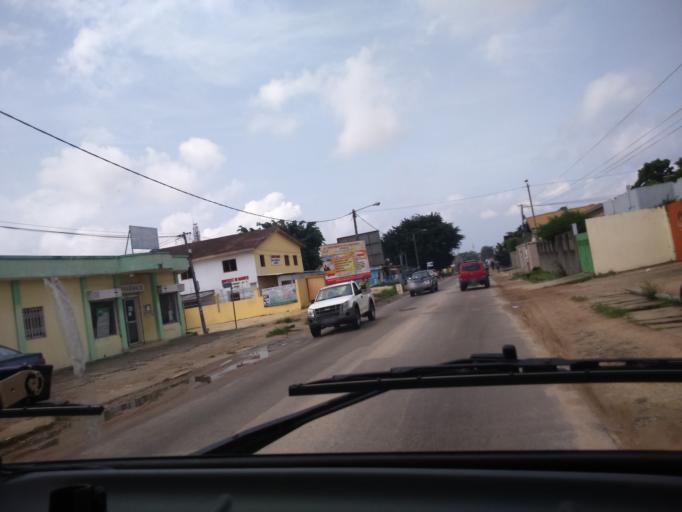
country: CI
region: Lagunes
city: Abobo
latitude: 5.3641
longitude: -3.9792
